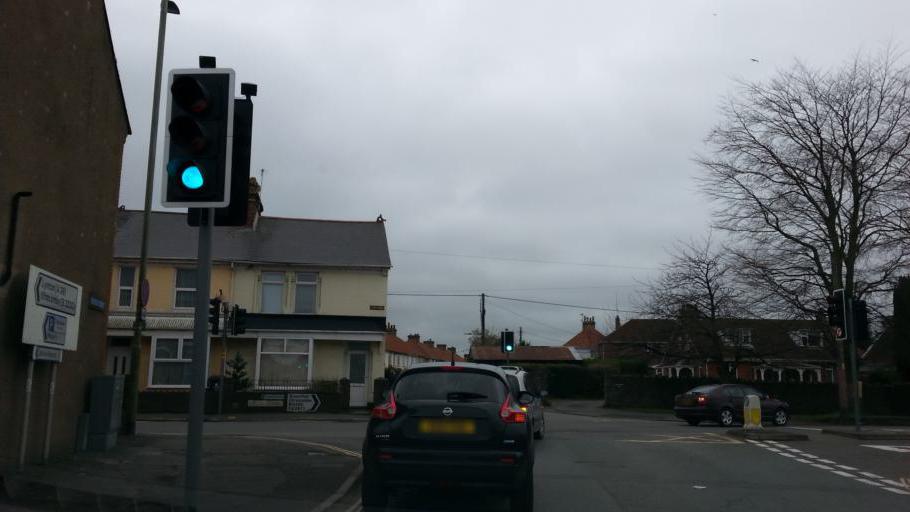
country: GB
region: England
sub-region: Devon
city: Barnstaple
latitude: 51.0840
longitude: -4.0657
